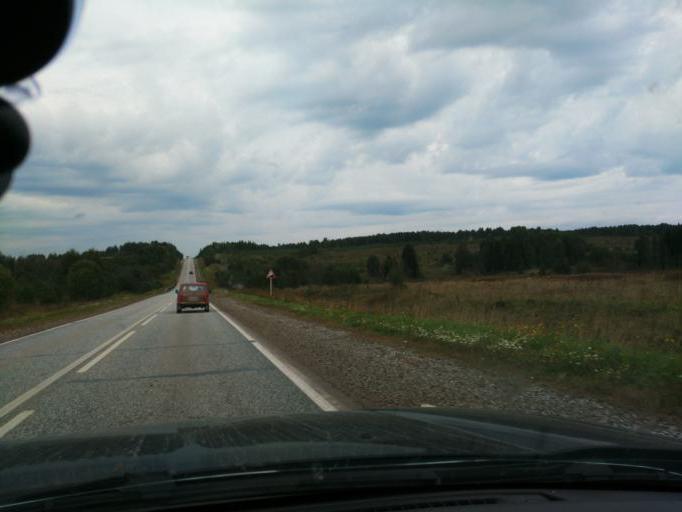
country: RU
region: Perm
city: Chernushka
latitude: 56.7644
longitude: 56.1344
